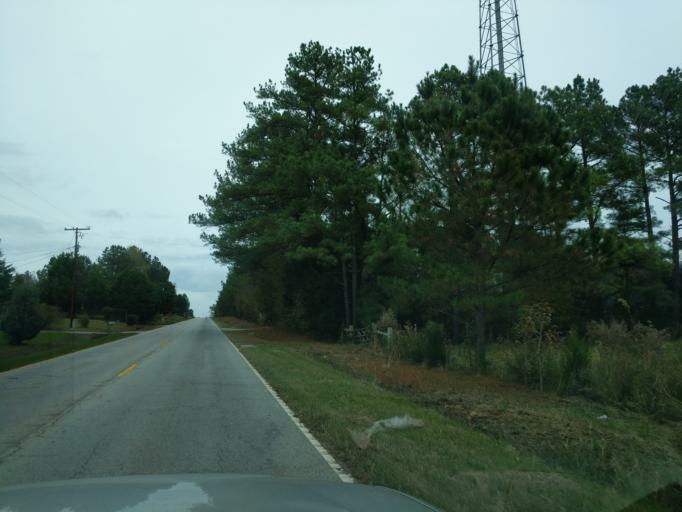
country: US
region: South Carolina
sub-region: Saluda County
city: Saluda
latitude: 34.0634
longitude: -81.7626
